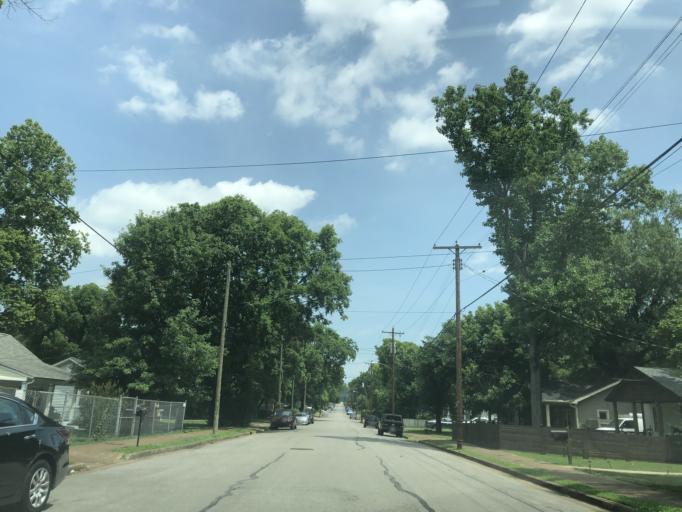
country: US
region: Tennessee
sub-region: Davidson County
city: Nashville
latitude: 36.1886
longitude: -86.7692
